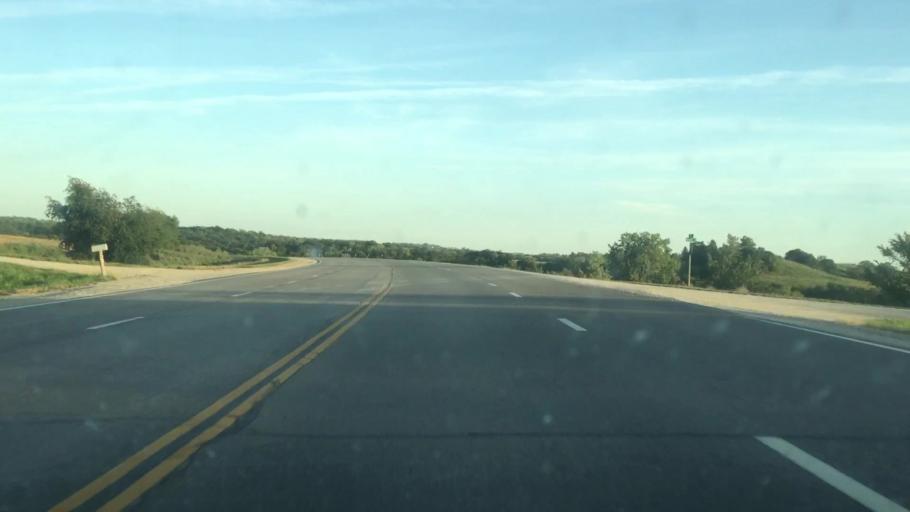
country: US
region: Kansas
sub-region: Atchison County
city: Atchison
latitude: 39.4885
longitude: -95.1301
